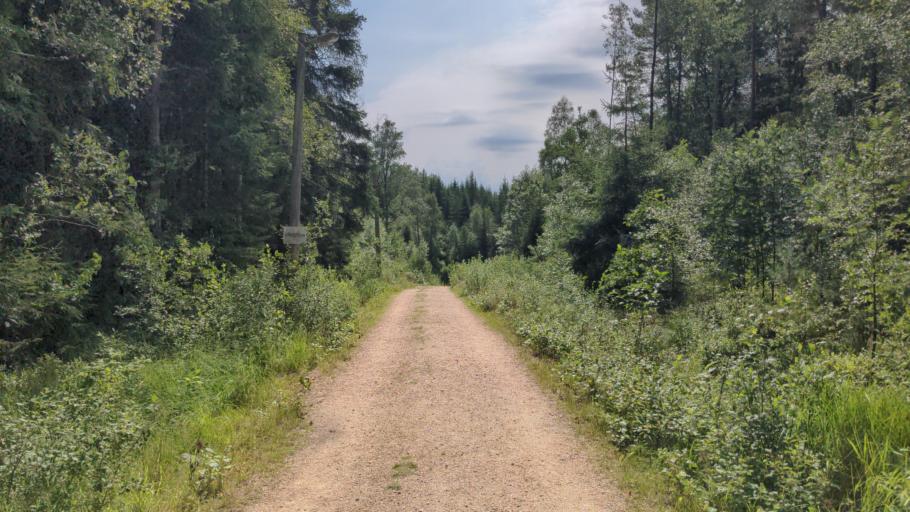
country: SE
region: Vaestra Goetaland
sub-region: Uddevalla Kommun
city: Uddevalla
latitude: 58.3810
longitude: 11.8294
